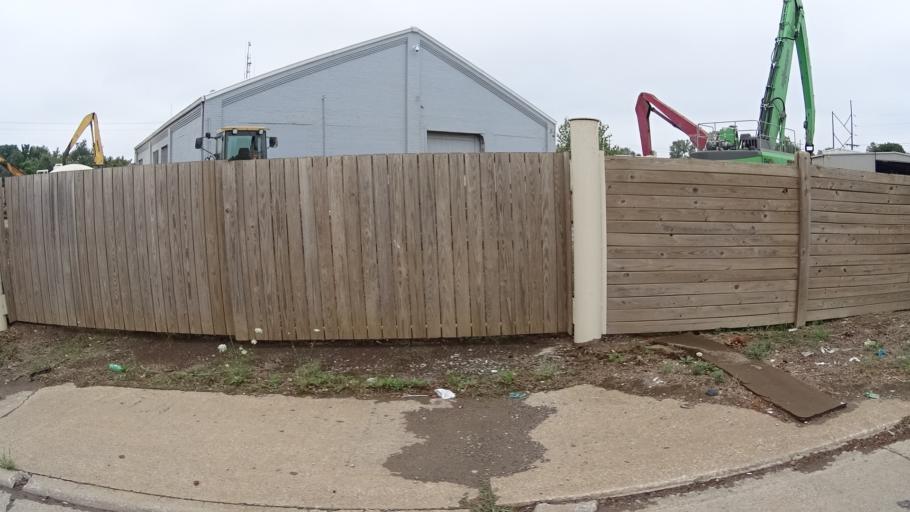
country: US
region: Ohio
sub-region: Erie County
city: Sandusky
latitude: 41.4396
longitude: -82.6958
